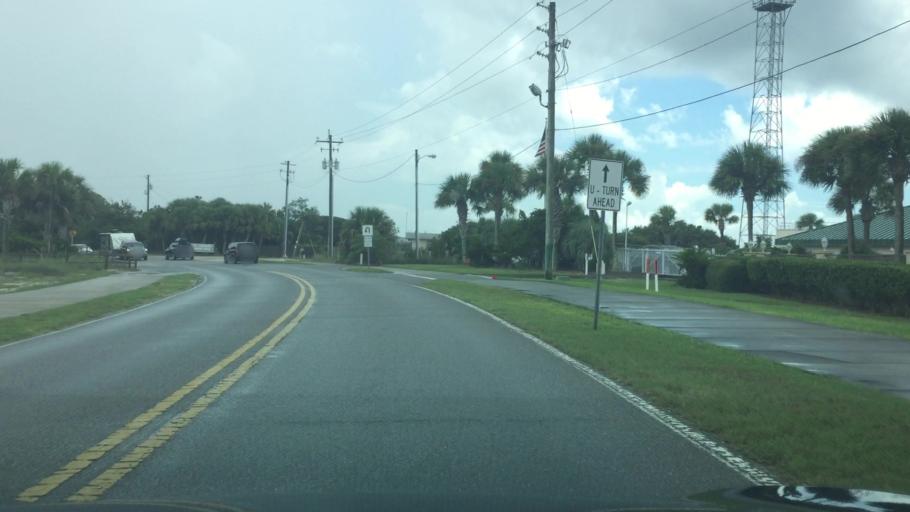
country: US
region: Florida
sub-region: Bay County
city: Lower Grand Lagoon
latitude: 30.1351
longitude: -85.7452
